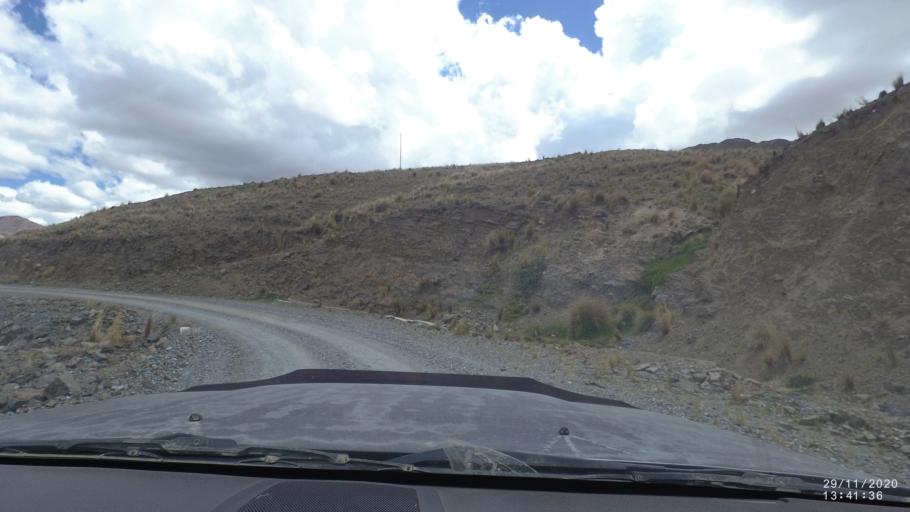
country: BO
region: Cochabamba
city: Cochabamba
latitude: -17.1324
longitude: -66.3242
